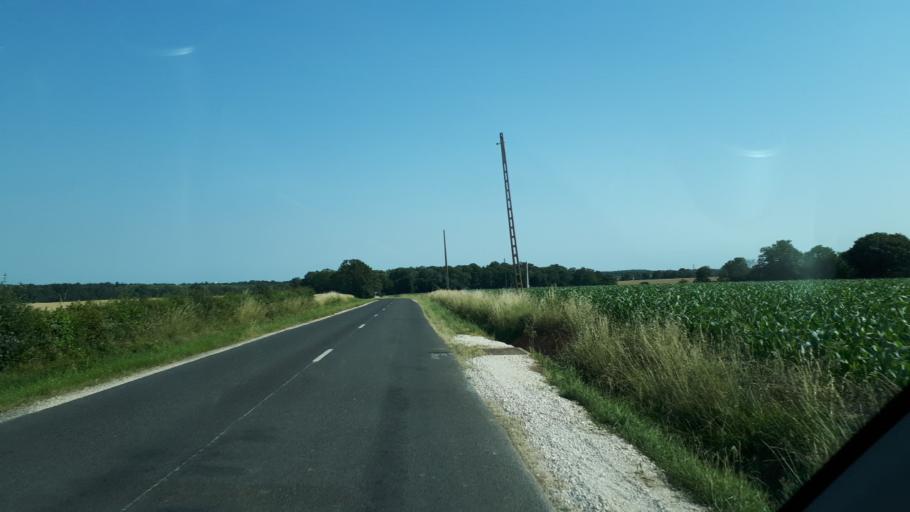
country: FR
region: Centre
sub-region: Departement du Loir-et-Cher
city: La Ville-aux-Clercs
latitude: 47.9419
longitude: 1.0812
